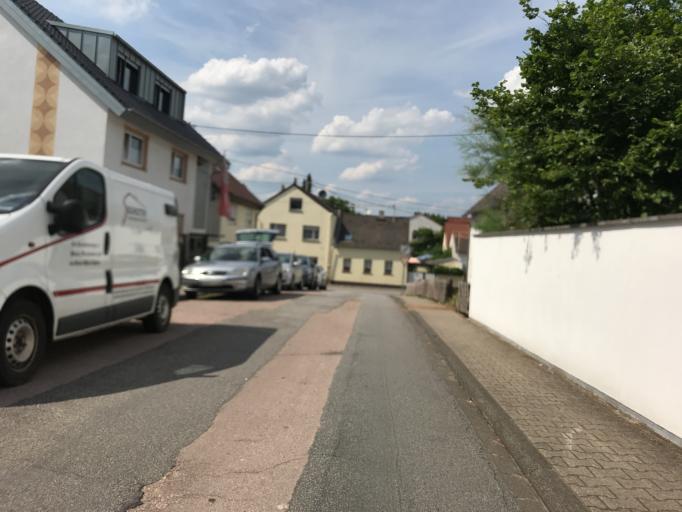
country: DE
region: Rheinland-Pfalz
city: Wackernheim
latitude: 49.9965
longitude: 8.1215
